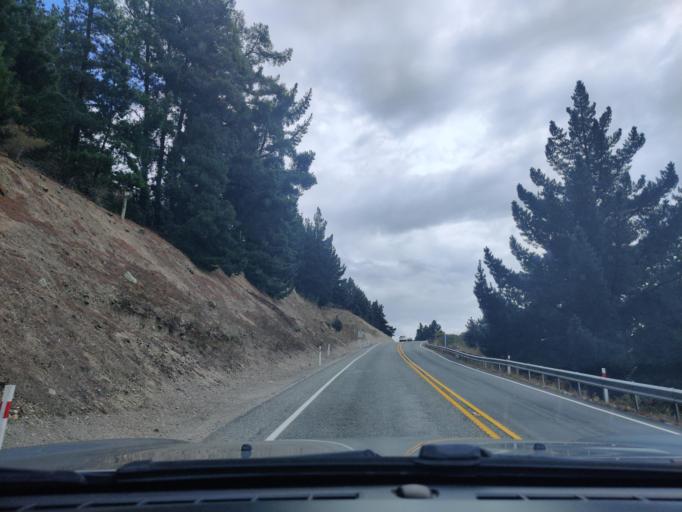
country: NZ
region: Otago
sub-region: Queenstown-Lakes District
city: Wanaka
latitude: -44.7319
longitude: 169.2549
